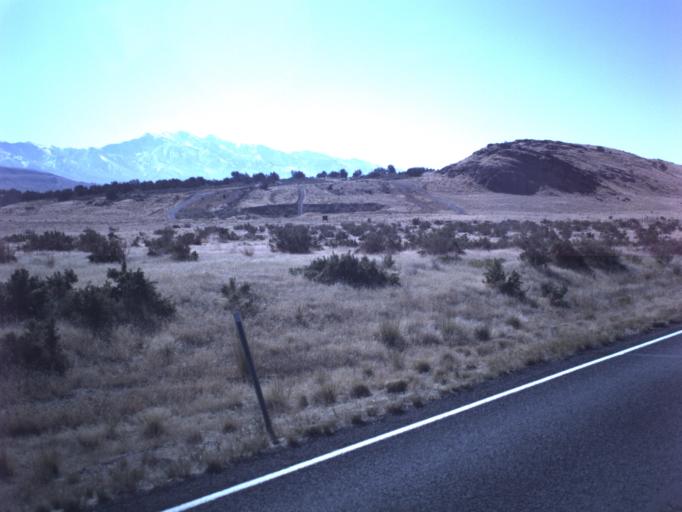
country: US
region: Utah
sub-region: Tooele County
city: Grantsville
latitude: 40.6171
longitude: -112.7025
